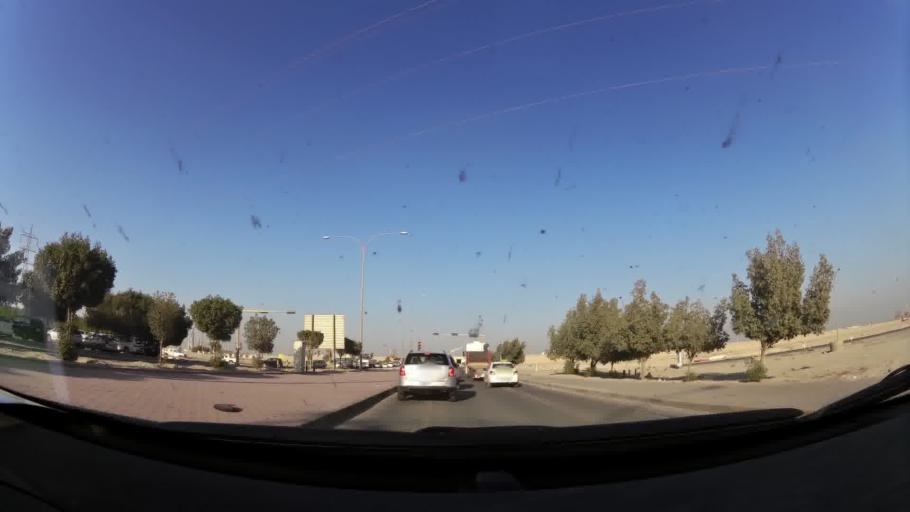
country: KW
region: Al Ahmadi
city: Al Fahahil
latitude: 29.0075
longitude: 48.1295
